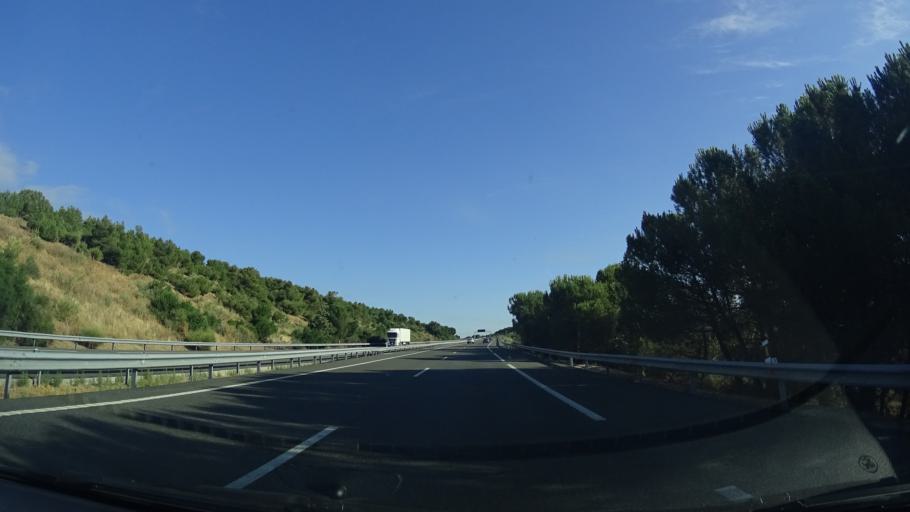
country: ES
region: Castille and Leon
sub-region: Provincia de Avila
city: Sanchidrian
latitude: 40.8708
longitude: -4.5667
